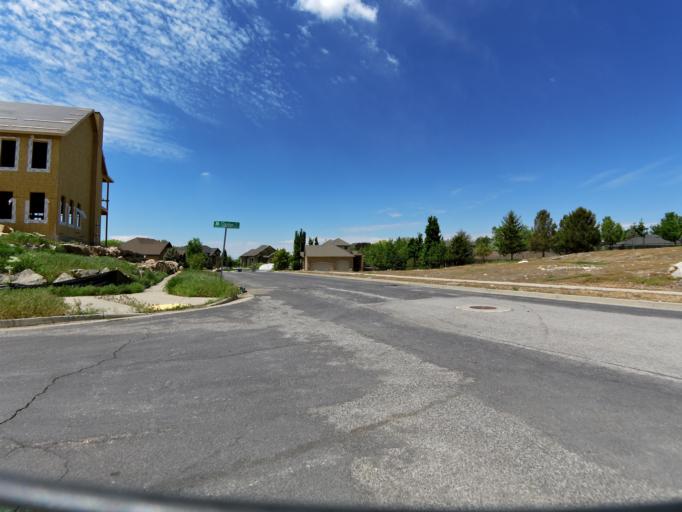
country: US
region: Utah
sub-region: Weber County
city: Uintah
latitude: 41.1751
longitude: -111.9335
